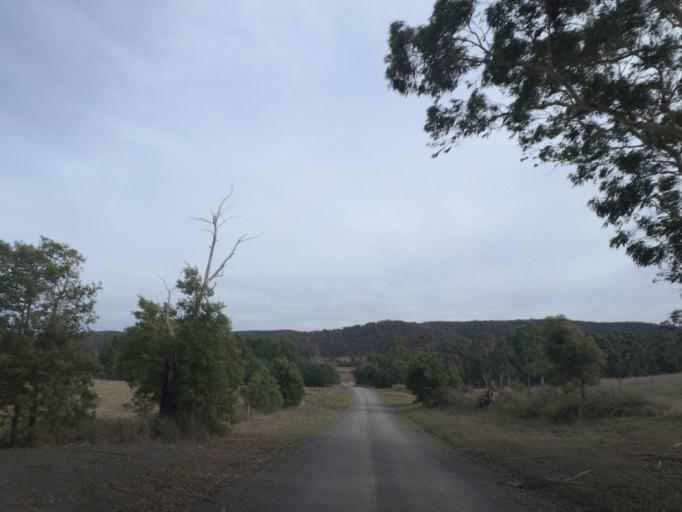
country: AU
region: Victoria
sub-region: Yarra Ranges
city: Yarra Glen
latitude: -37.5945
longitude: 145.3814
